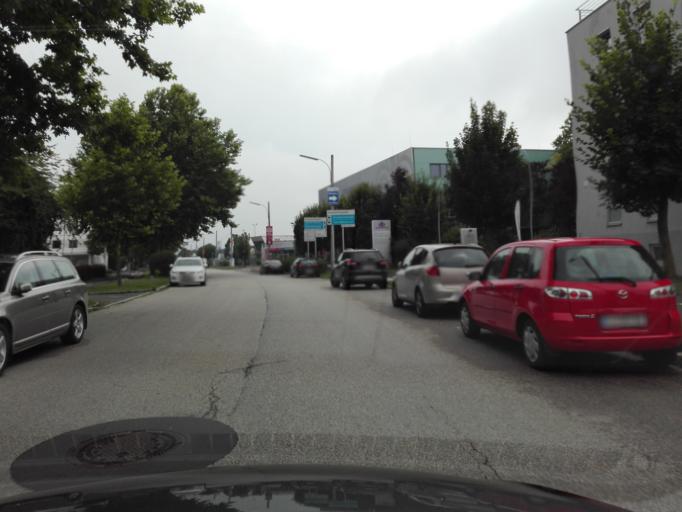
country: AT
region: Upper Austria
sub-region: Politischer Bezirk Linz-Land
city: Ansfelden
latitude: 48.2432
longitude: 14.2936
